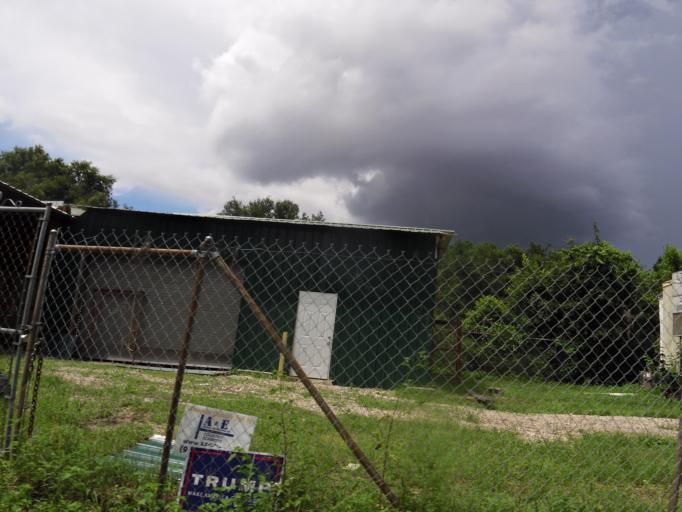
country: US
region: Florida
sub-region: Duval County
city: Jacksonville
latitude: 30.3681
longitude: -81.6362
